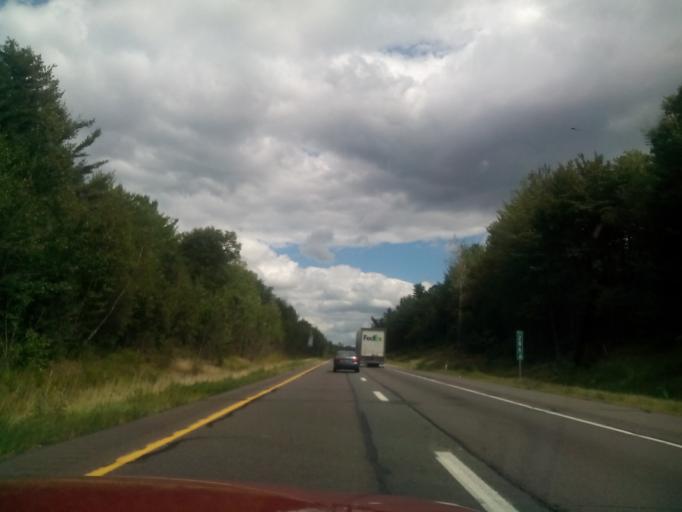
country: US
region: Pennsylvania
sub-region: Monroe County
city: Pocono Pines
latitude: 41.0781
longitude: -75.5212
